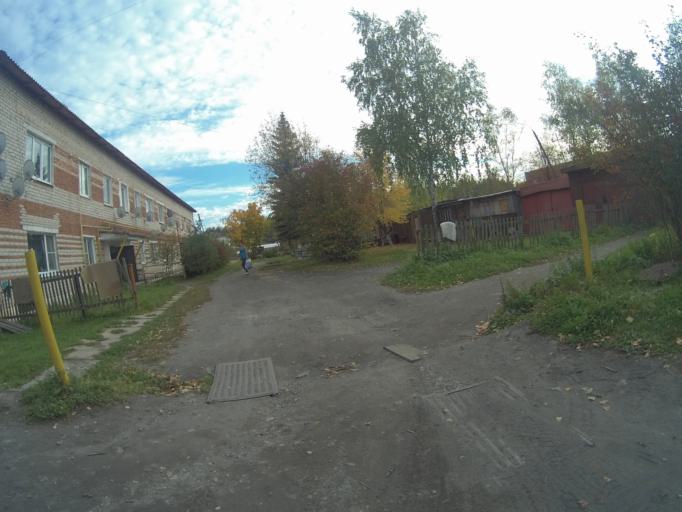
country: RU
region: Vladimir
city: Golovino
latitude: 55.9590
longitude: 40.4274
